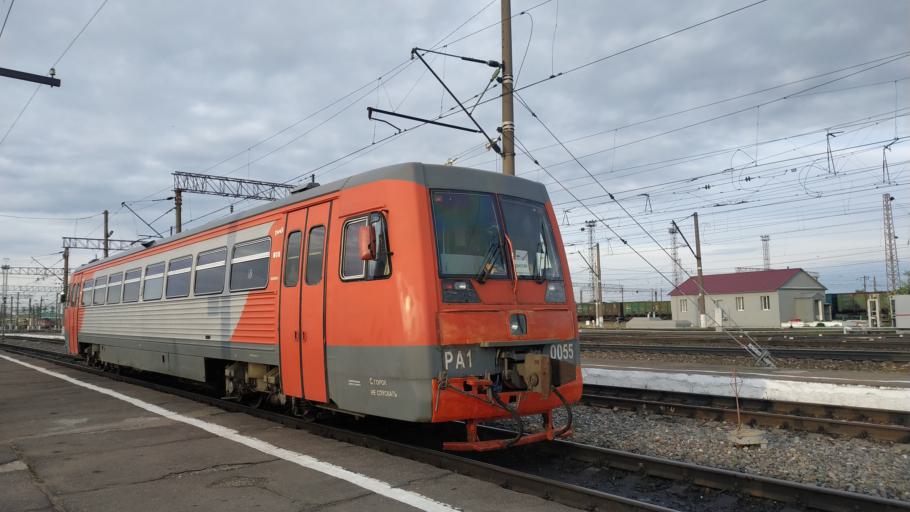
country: RU
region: Smolensk
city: Vyaz'ma
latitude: 55.2004
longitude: 34.3189
